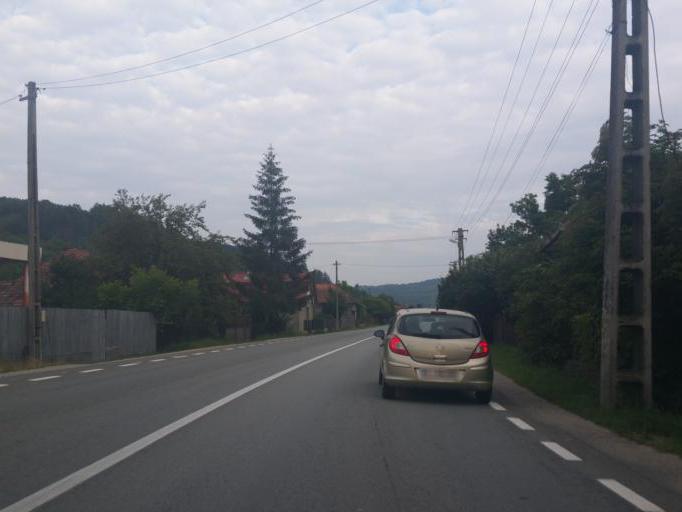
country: RO
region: Salaj
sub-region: Comuna Sanmihaiu Almasului
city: Sanmihaiu Almasului
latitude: 46.9561
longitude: 23.3464
